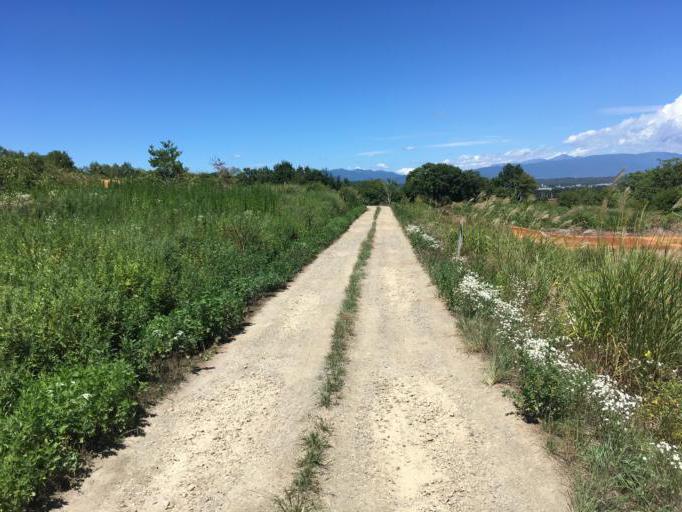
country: JP
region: Yamagata
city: Yonezawa
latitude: 37.9697
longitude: 140.0594
